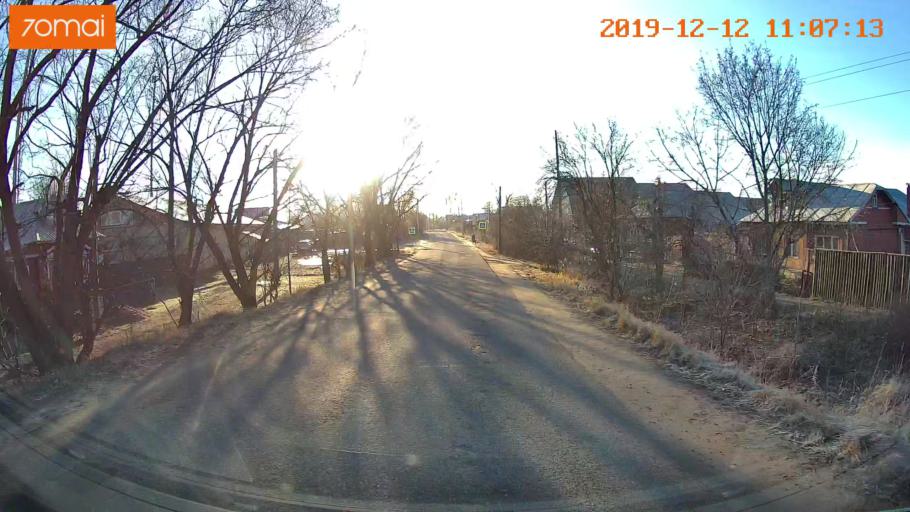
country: RU
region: Ivanovo
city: Kokhma
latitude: 56.9383
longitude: 41.0890
